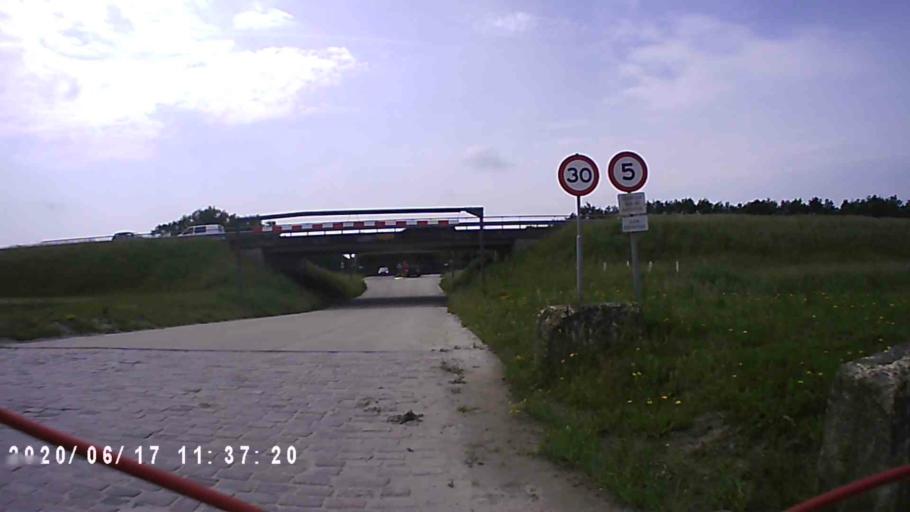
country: NL
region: Groningen
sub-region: Gemeente De Marne
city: Ulrum
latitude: 53.3656
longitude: 6.2679
